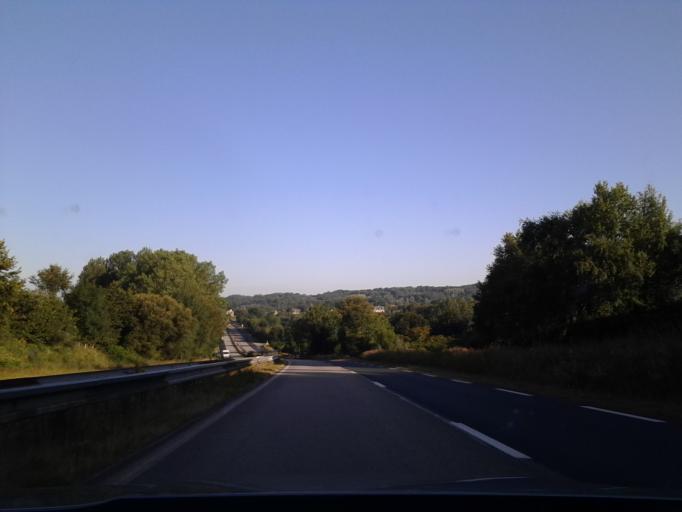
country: FR
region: Lower Normandy
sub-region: Departement de la Manche
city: Brix
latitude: 49.5379
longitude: -1.5387
